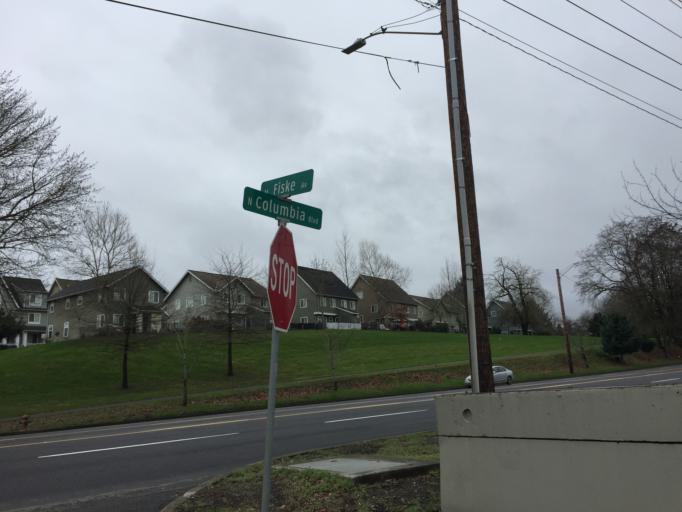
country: US
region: Washington
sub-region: Clark County
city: Vancouver
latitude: 45.5940
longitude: -122.7167
